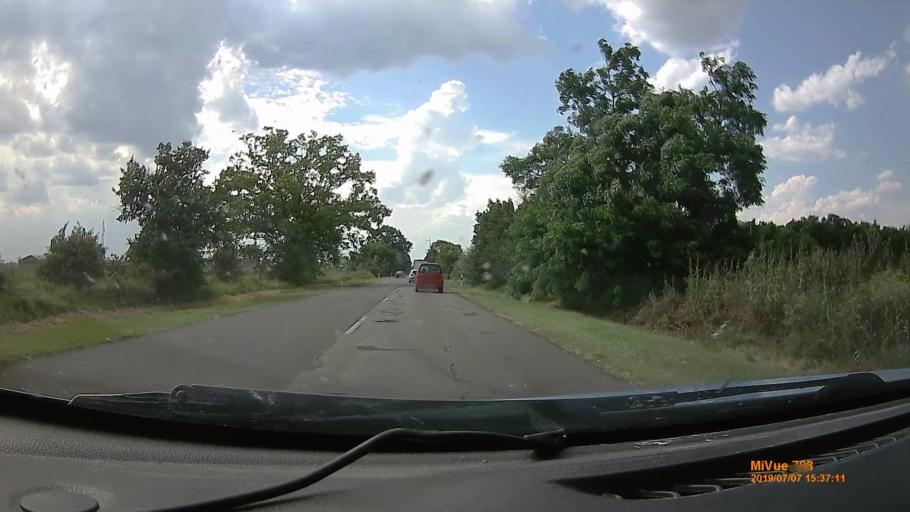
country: HU
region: Jasz-Nagykun-Szolnok
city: Jaszbereny
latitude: 47.4840
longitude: 19.9522
